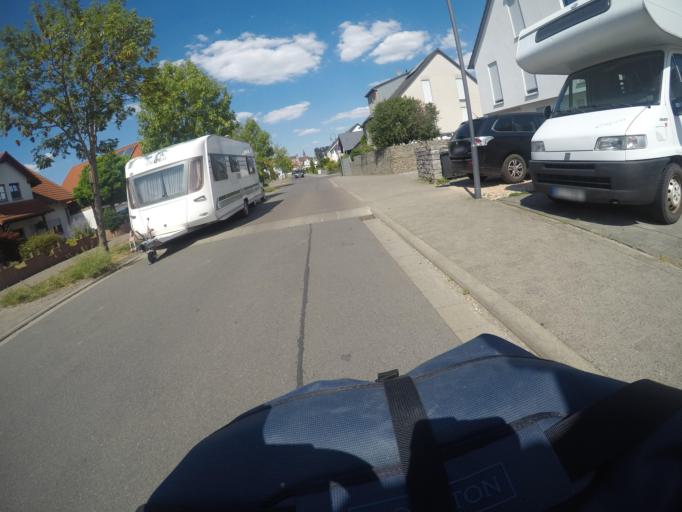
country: DE
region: Rheinland-Pfalz
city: Dienheim
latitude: 49.8426
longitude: 8.3537
